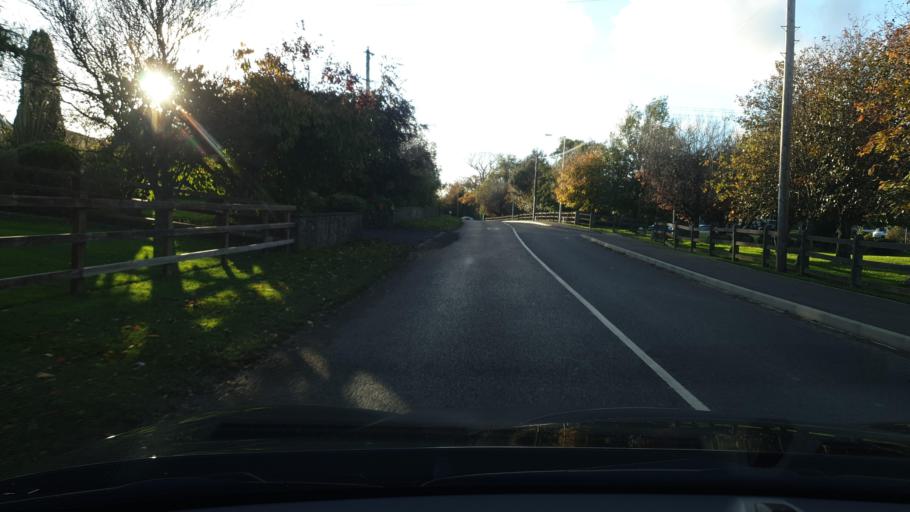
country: IE
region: Leinster
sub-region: An Mhi
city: Stamullin
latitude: 53.6263
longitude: -6.2695
